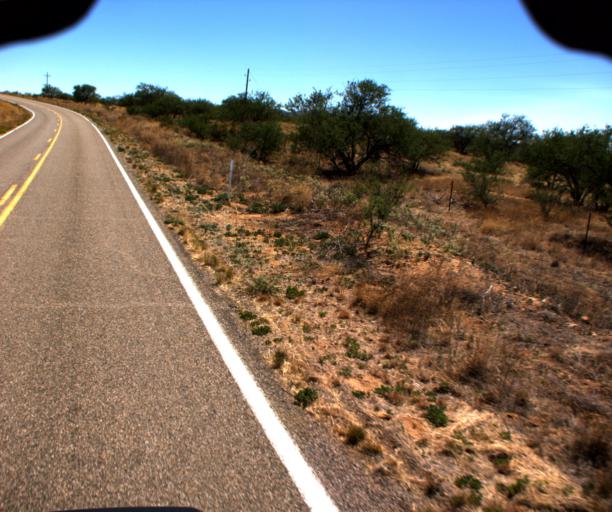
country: US
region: Arizona
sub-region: Pima County
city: Sells
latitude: 31.5796
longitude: -111.5368
